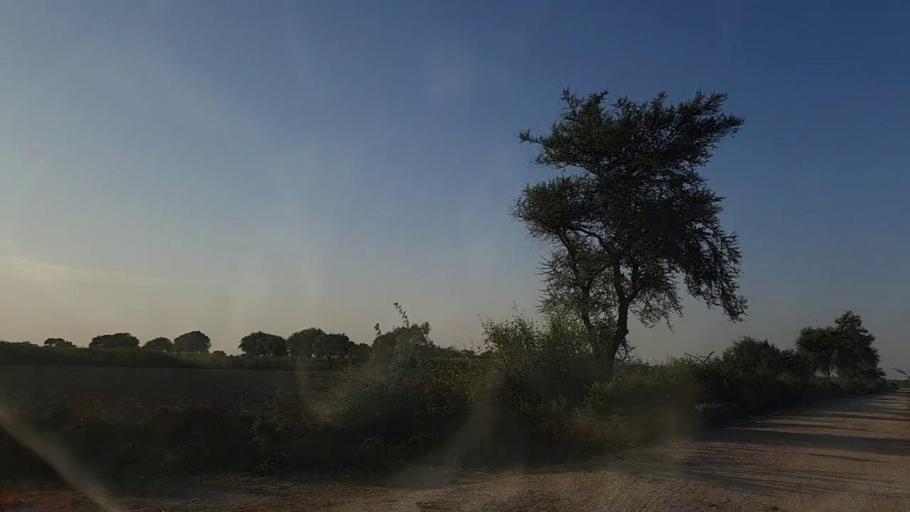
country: PK
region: Sindh
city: Jati
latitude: 24.4162
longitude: 68.1739
